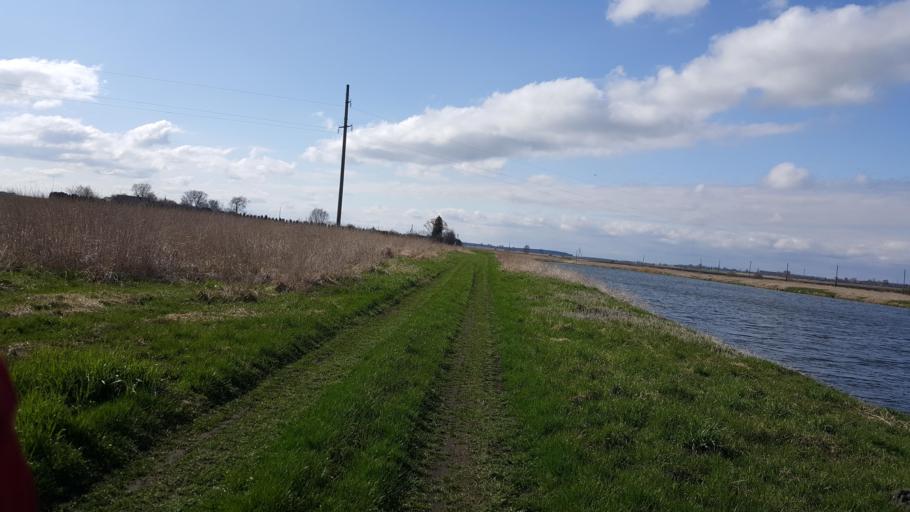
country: BY
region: Brest
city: Kamyanyets
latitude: 52.4059
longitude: 23.7791
